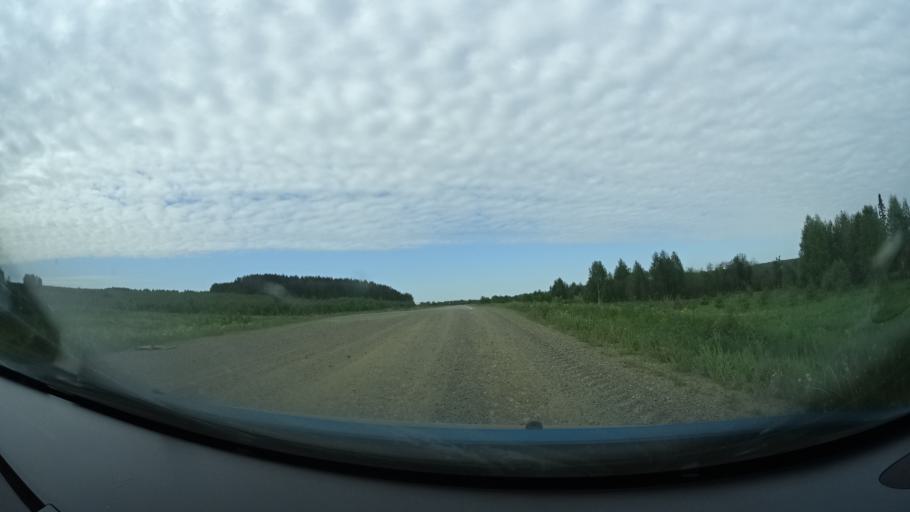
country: RU
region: Perm
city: Kuyeda
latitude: 56.5254
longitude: 55.6306
